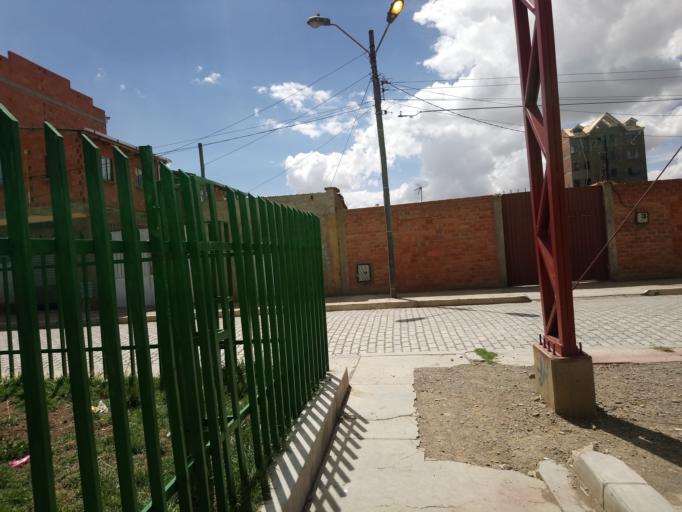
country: BO
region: La Paz
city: La Paz
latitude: -16.5567
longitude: -68.1924
